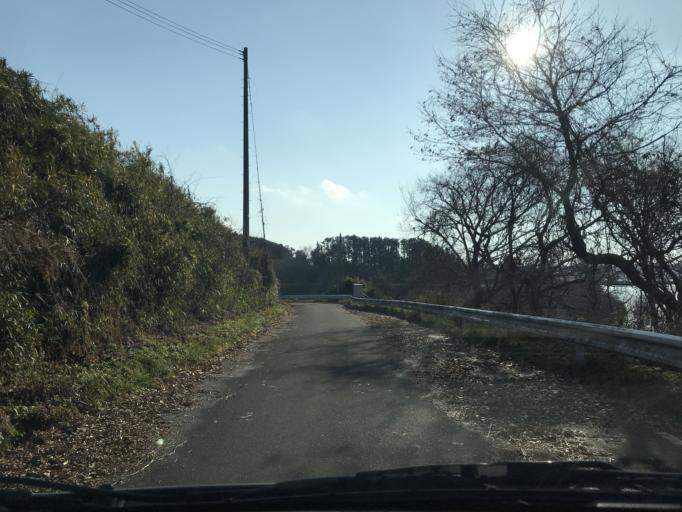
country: JP
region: Miyagi
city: Wakuya
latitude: 38.6891
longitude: 141.1287
